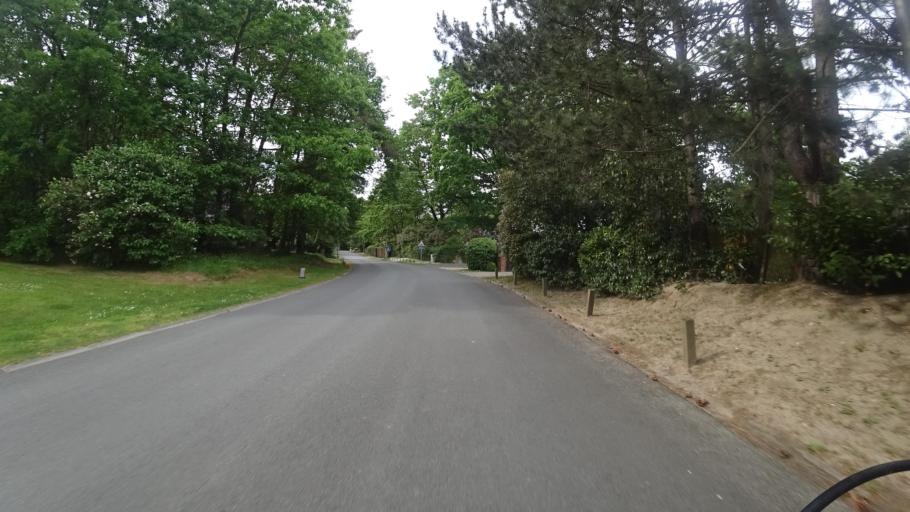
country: BE
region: Wallonia
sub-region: Province du Brabant Wallon
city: Grez-Doiceau
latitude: 50.7321
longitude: 4.6823
